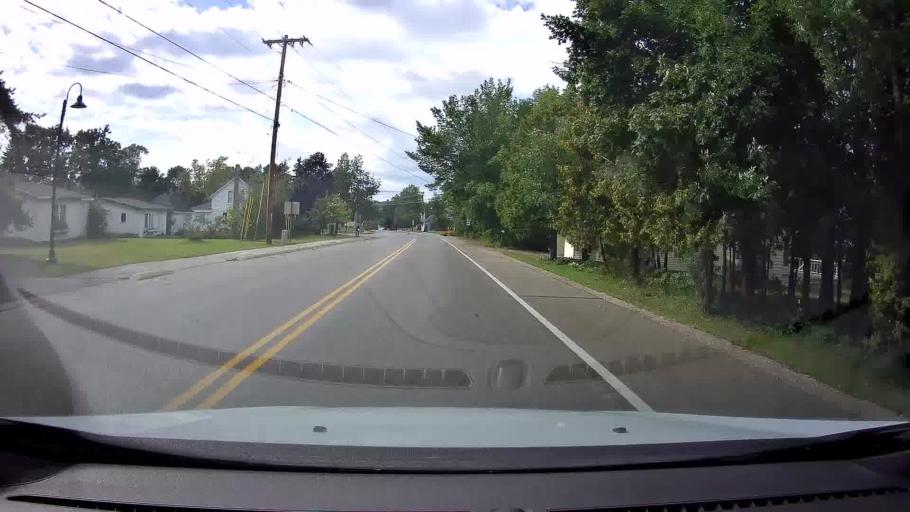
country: US
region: Wisconsin
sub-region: Door County
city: Sturgeon Bay
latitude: 45.0552
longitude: -87.2803
